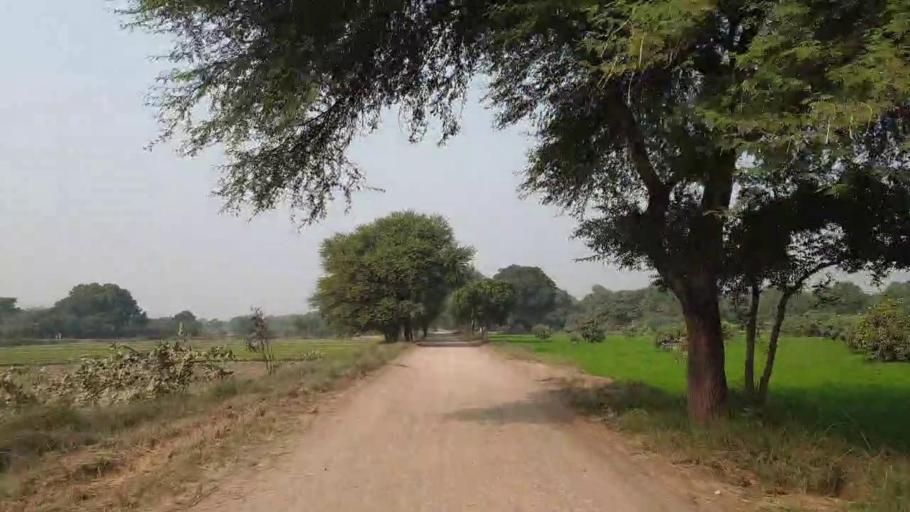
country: PK
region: Sindh
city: Tando Muhammad Khan
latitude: 25.2147
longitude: 68.5562
